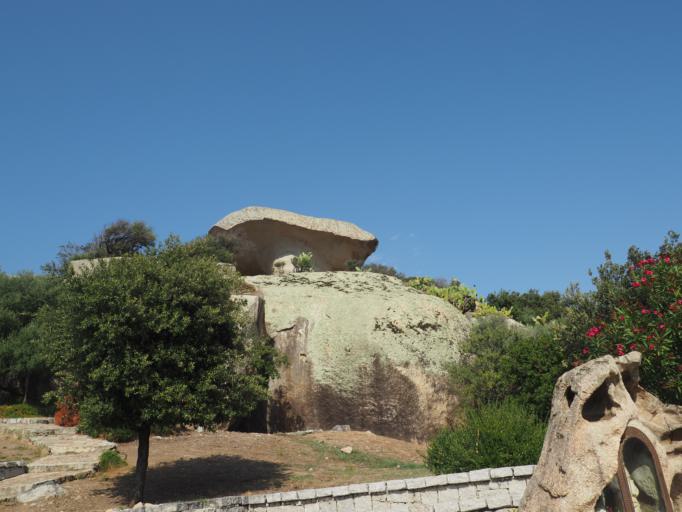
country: IT
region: Sardinia
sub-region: Provincia di Olbia-Tempio
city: Arzachena
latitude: 41.0793
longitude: 9.3920
